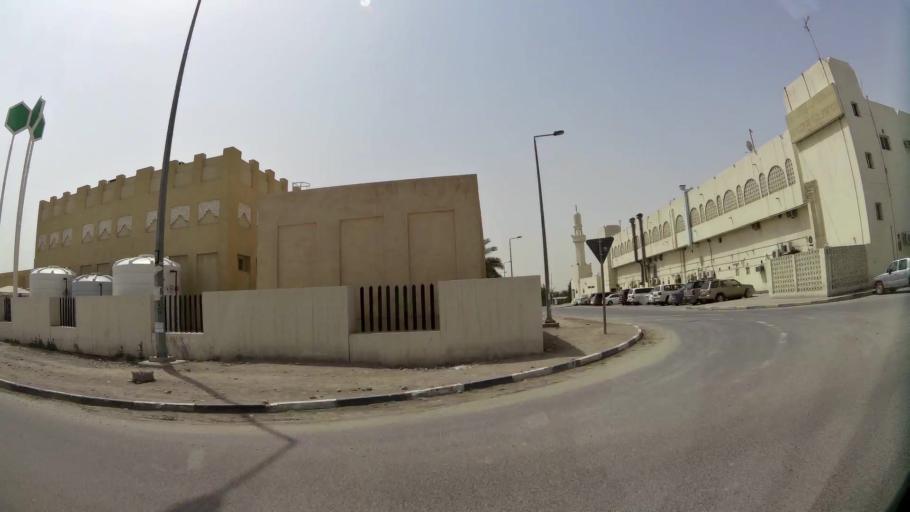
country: QA
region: Baladiyat ar Rayyan
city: Ar Rayyan
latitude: 25.2394
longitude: 51.4307
